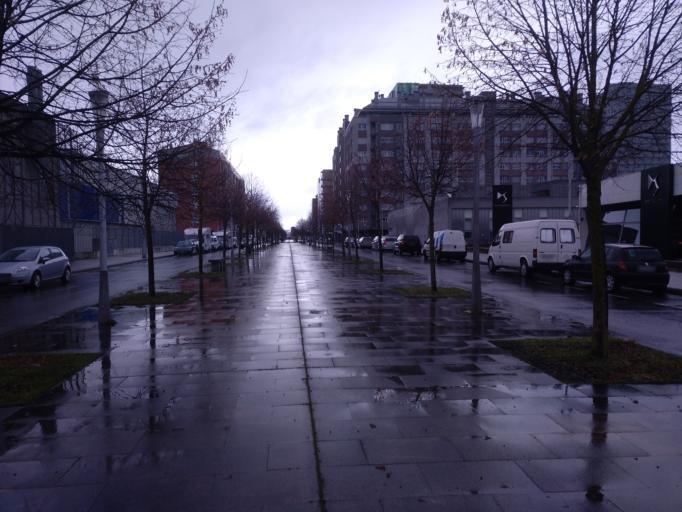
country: ES
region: Basque Country
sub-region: Provincia de Alava
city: Gasteiz / Vitoria
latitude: 42.8487
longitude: -2.6530
